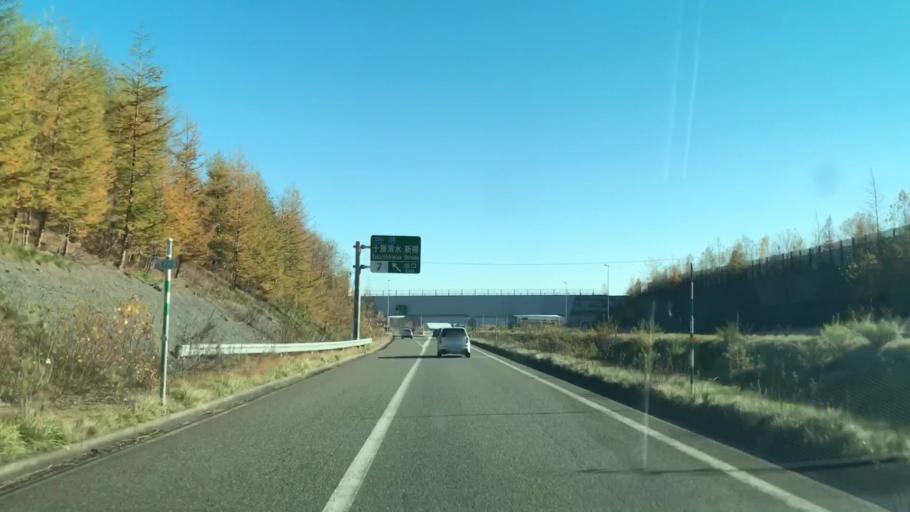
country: JP
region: Hokkaido
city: Otofuke
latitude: 42.9976
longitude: 142.8532
